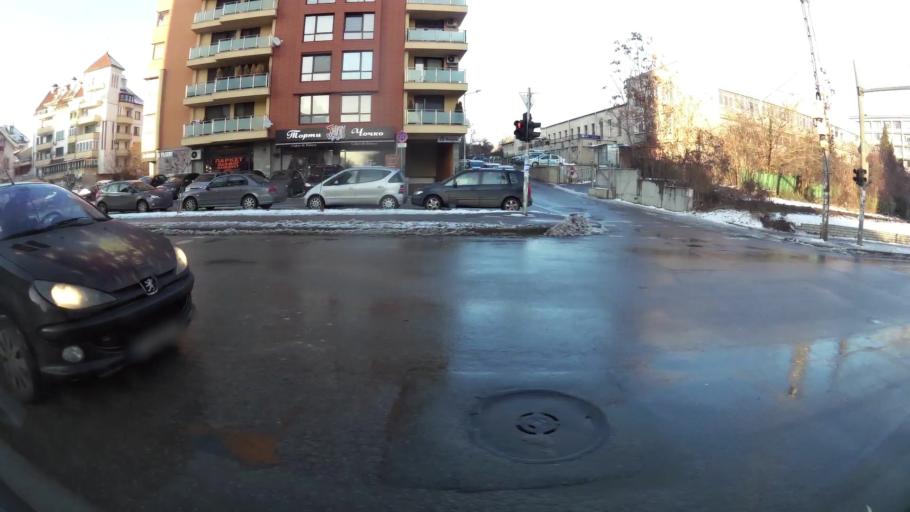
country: BG
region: Sofia-Capital
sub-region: Stolichna Obshtina
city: Sofia
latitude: 42.6822
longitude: 23.3679
